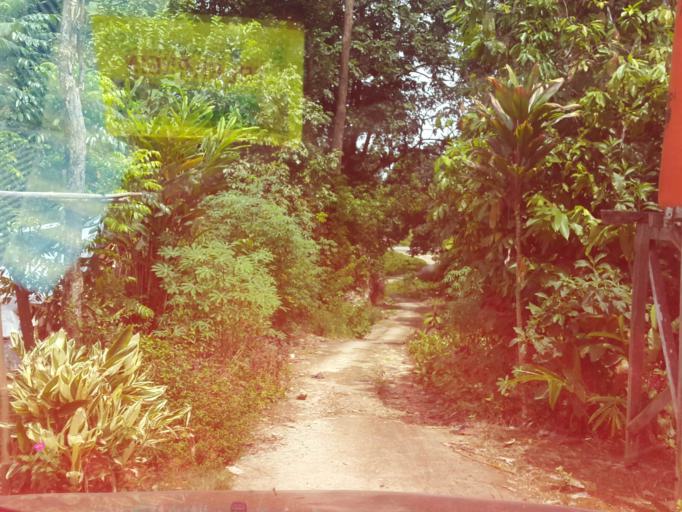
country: MY
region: Sarawak
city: Kuching
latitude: 0.8683
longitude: 110.4071
